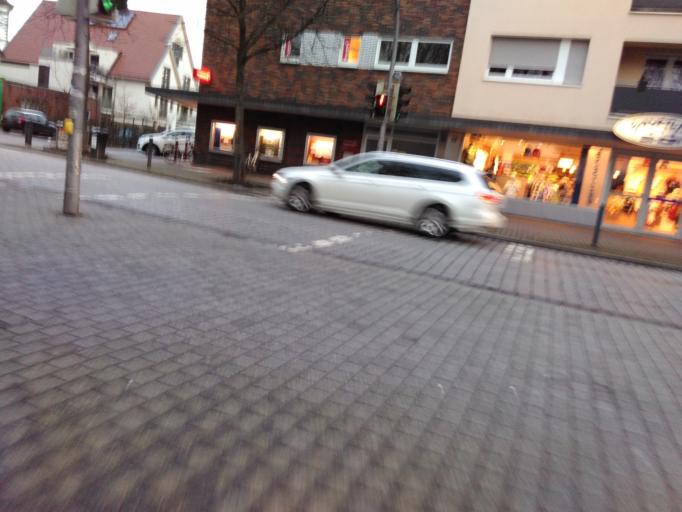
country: DE
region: North Rhine-Westphalia
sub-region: Regierungsbezirk Detmold
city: Verl
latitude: 51.8834
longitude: 8.5074
